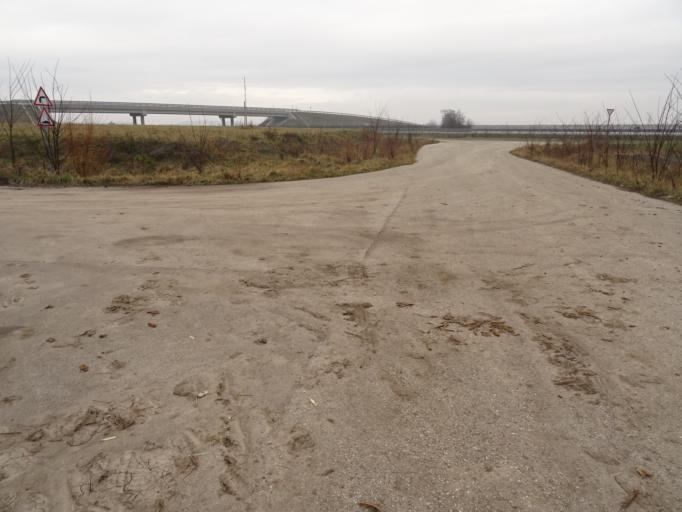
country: HU
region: Gyor-Moson-Sopron
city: Kony
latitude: 47.6381
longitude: 17.3732
